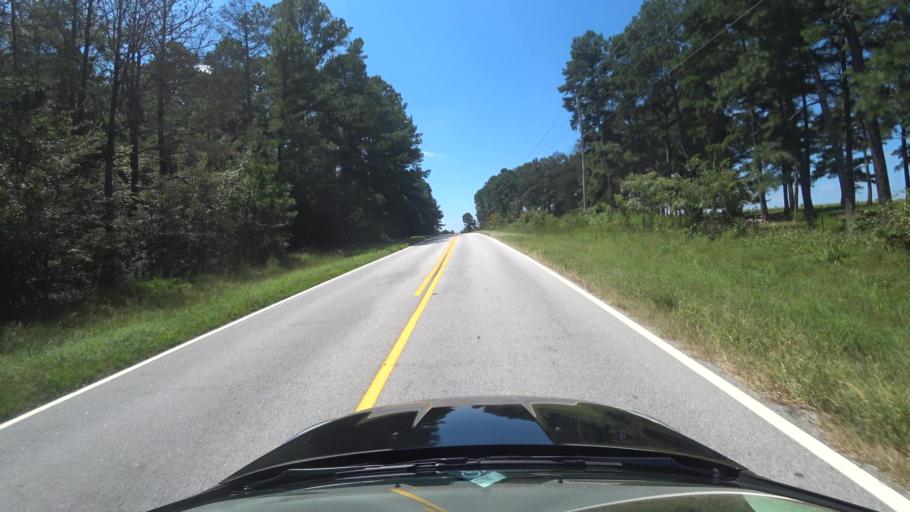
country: US
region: Georgia
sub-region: Newton County
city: Oxford
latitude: 33.6345
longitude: -83.8167
